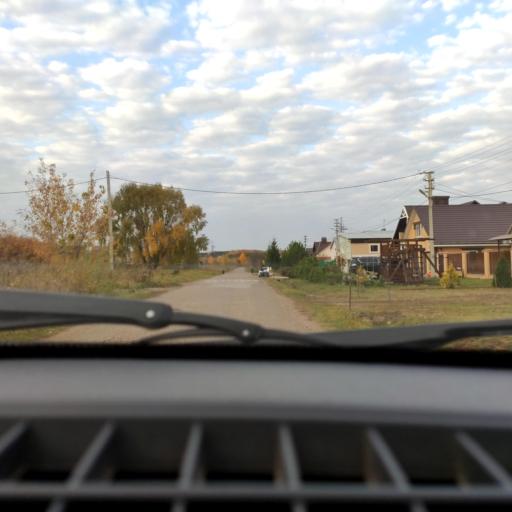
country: RU
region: Bashkortostan
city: Avdon
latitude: 54.6909
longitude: 55.7881
